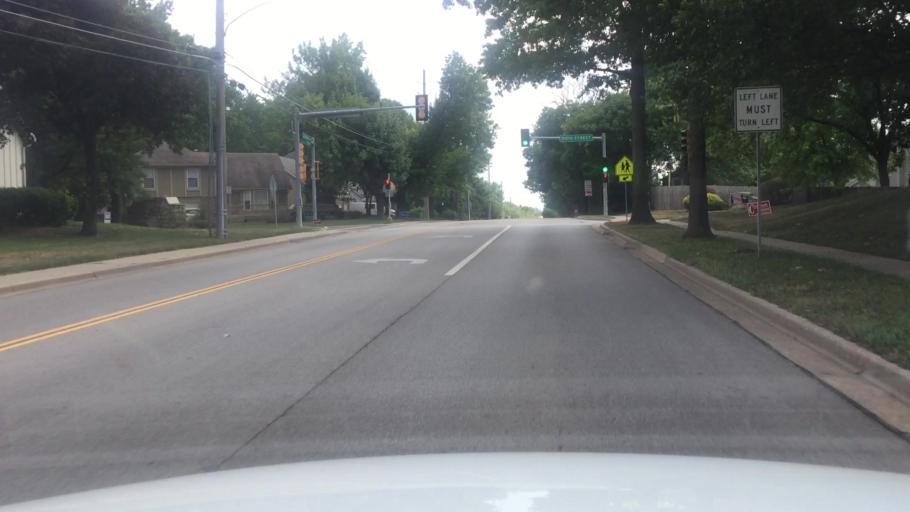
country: US
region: Kansas
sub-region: Johnson County
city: Lenexa
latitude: 38.9653
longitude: -94.7610
